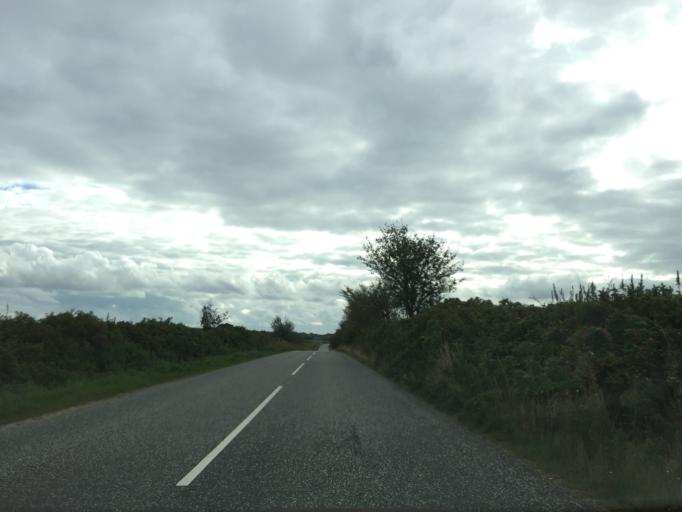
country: DK
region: Central Jutland
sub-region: Favrskov Kommune
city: Hammel
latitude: 56.2412
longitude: 9.7548
